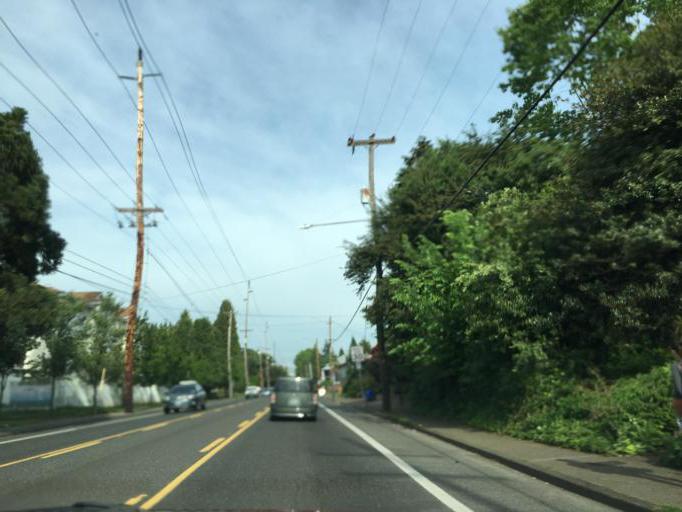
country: US
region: Oregon
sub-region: Multnomah County
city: Lents
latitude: 45.5054
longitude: -122.5989
